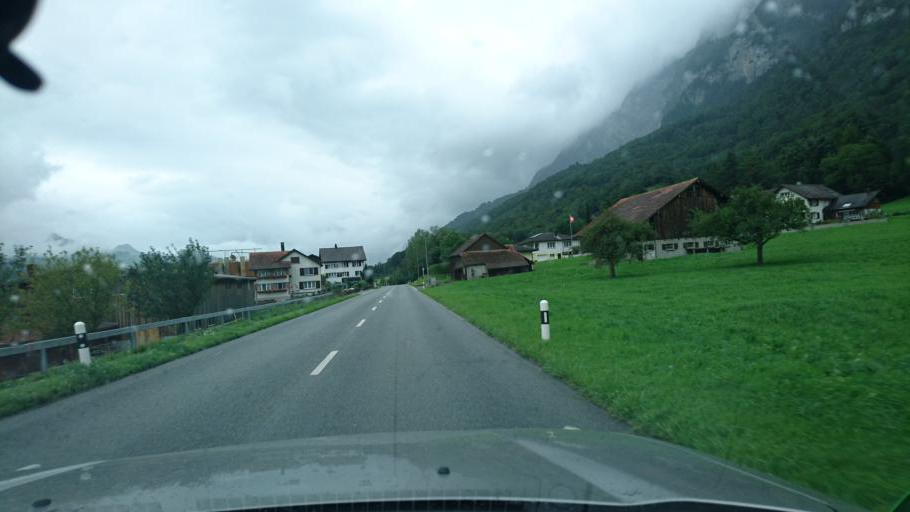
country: CH
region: Saint Gallen
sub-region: Wahlkreis Sarganserland
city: Flums
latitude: 47.0721
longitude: 9.3923
